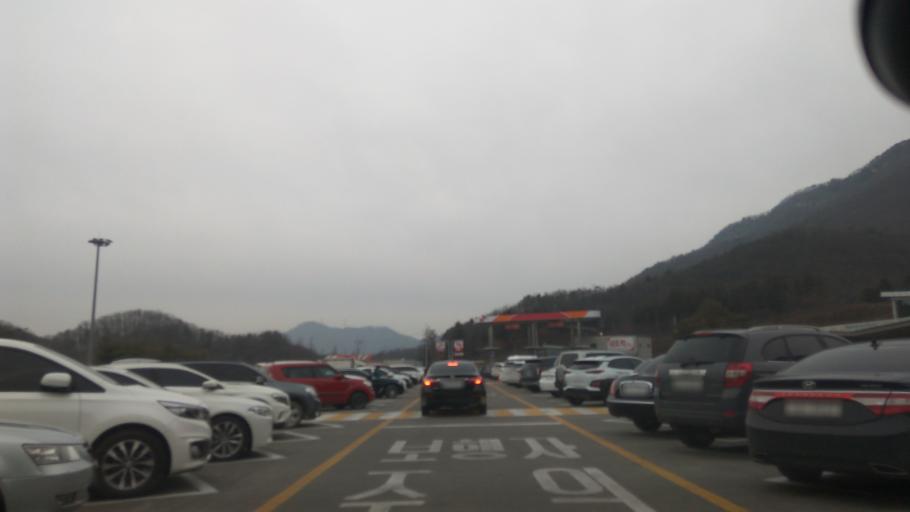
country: KR
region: Gyeonggi-do
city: Cheongpyeong
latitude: 37.7016
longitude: 127.5458
